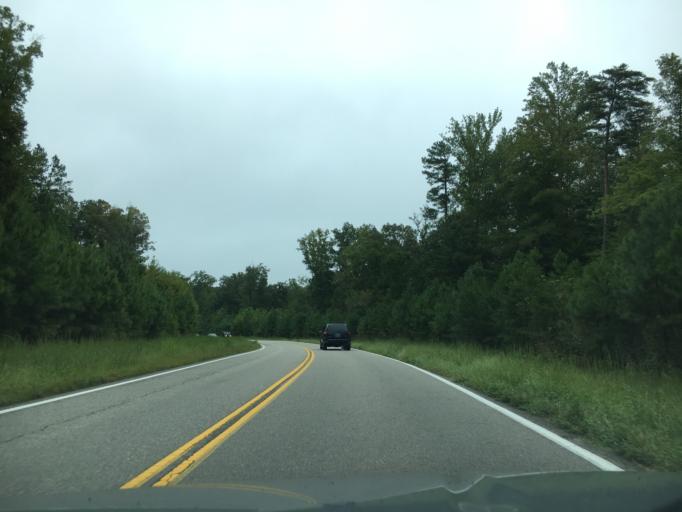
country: US
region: Virginia
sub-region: Chesterfield County
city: Woodlake
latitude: 37.5001
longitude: -77.7781
